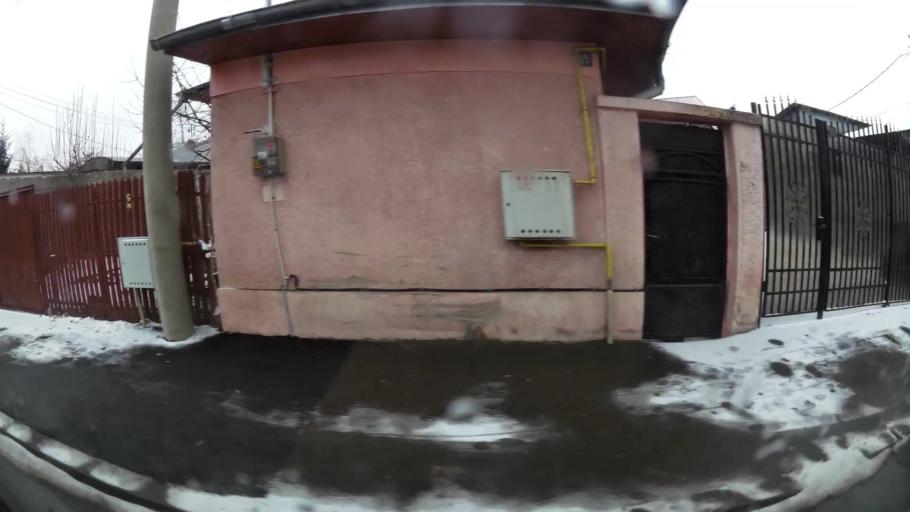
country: RO
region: Prahova
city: Ploiesti
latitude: 44.9485
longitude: 26.0273
